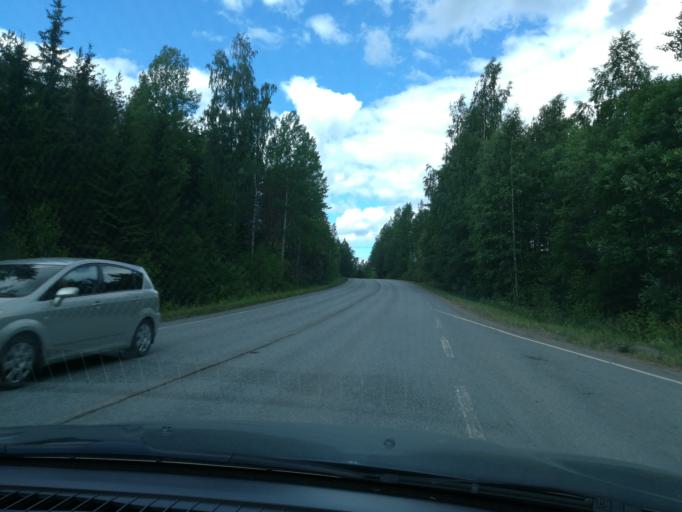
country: FI
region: Southern Savonia
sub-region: Mikkeli
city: Maentyharju
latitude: 61.4067
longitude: 26.8912
